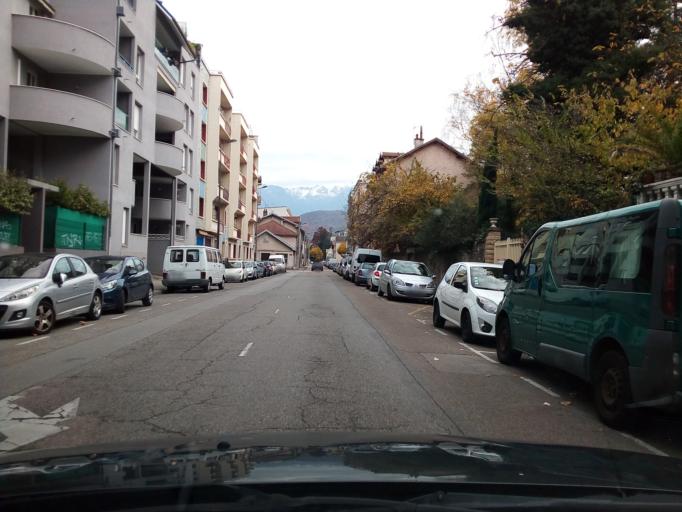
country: FR
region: Rhone-Alpes
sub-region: Departement de l'Isere
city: Grenoble
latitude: 45.1761
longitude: 5.7331
